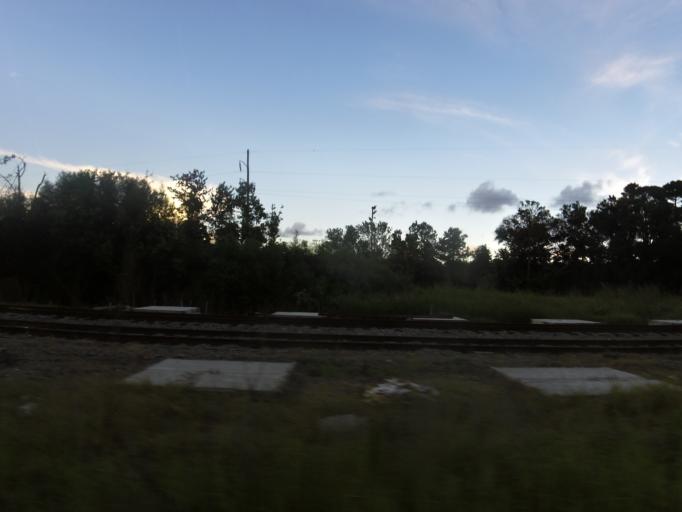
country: US
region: Georgia
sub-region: Camden County
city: St. Marys
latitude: 30.7361
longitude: -81.5533
